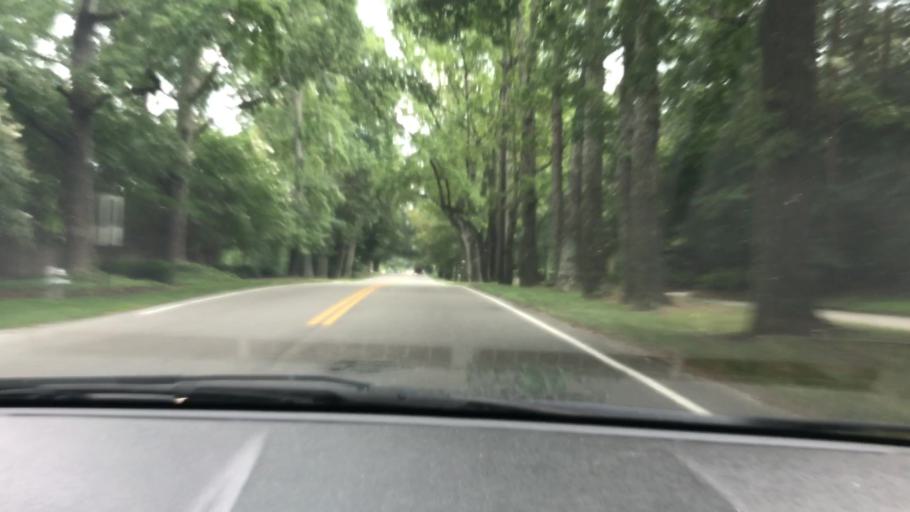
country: US
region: Virginia
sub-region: Henrico County
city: Dumbarton
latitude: 37.5642
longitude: -77.5060
